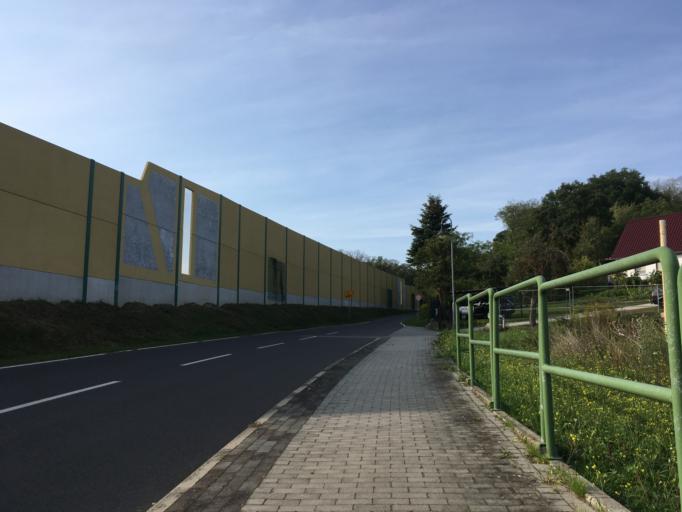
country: DE
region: Brandenburg
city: Brieskow-Finkenheerd
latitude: 52.2660
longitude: 14.5724
